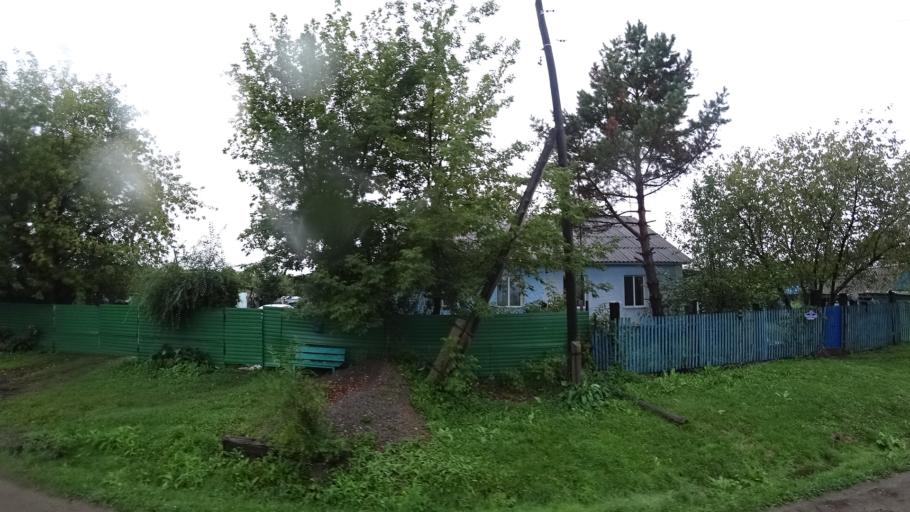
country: RU
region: Primorskiy
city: Monastyrishche
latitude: 44.2548
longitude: 132.4269
